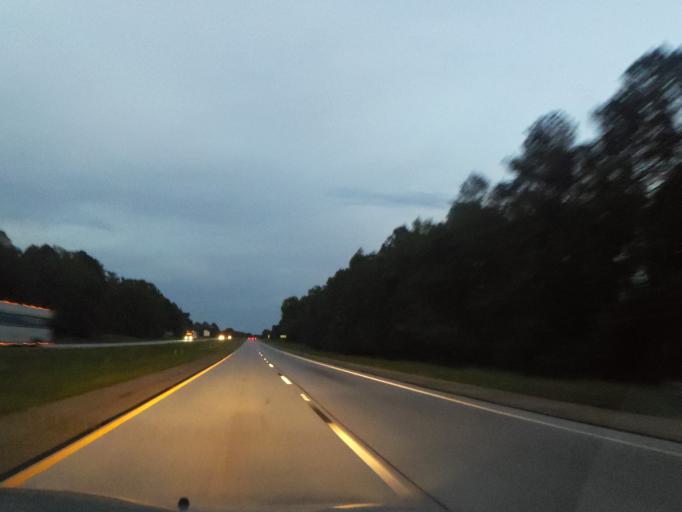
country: US
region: Georgia
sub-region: McDuffie County
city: Thomson
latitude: 33.5130
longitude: -82.4872
